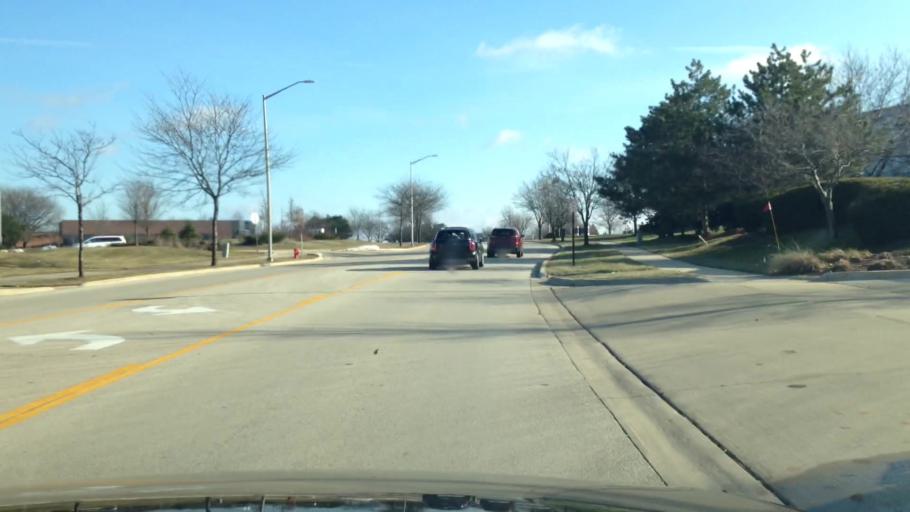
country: US
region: Illinois
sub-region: Cook County
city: Hoffman Estates
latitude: 42.0554
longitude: -88.0772
